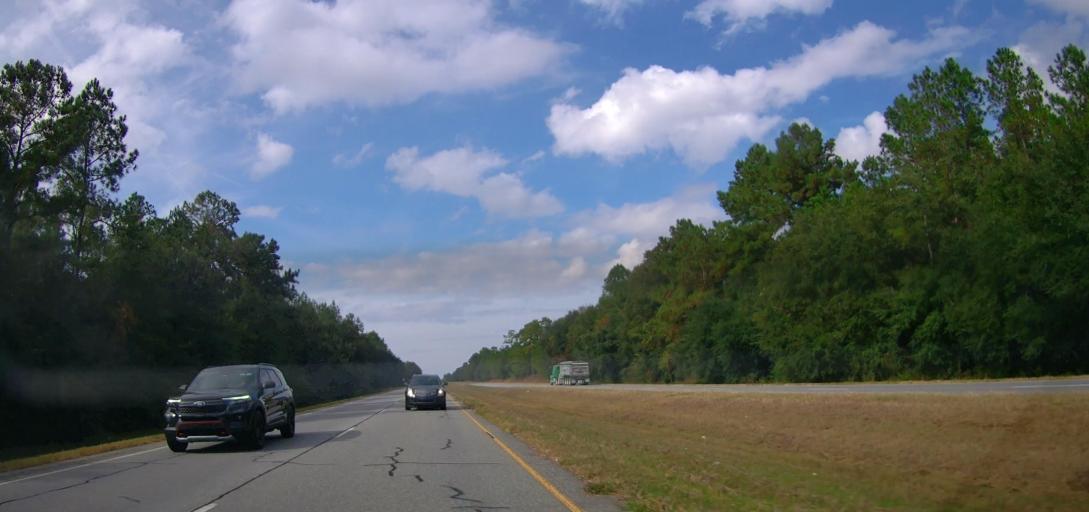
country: US
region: Georgia
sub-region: Mitchell County
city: Pelham
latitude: 31.1893
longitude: -84.1603
